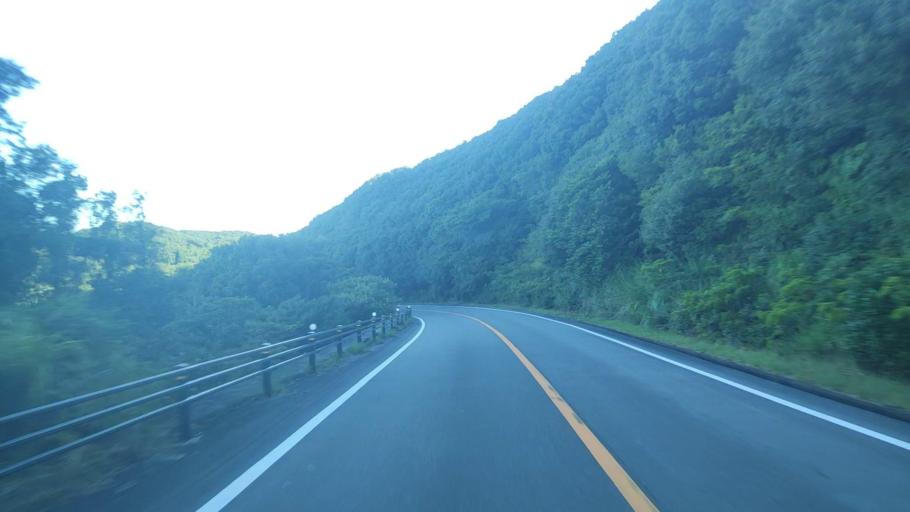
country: JP
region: Mie
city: Toba
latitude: 34.4246
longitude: 136.9147
